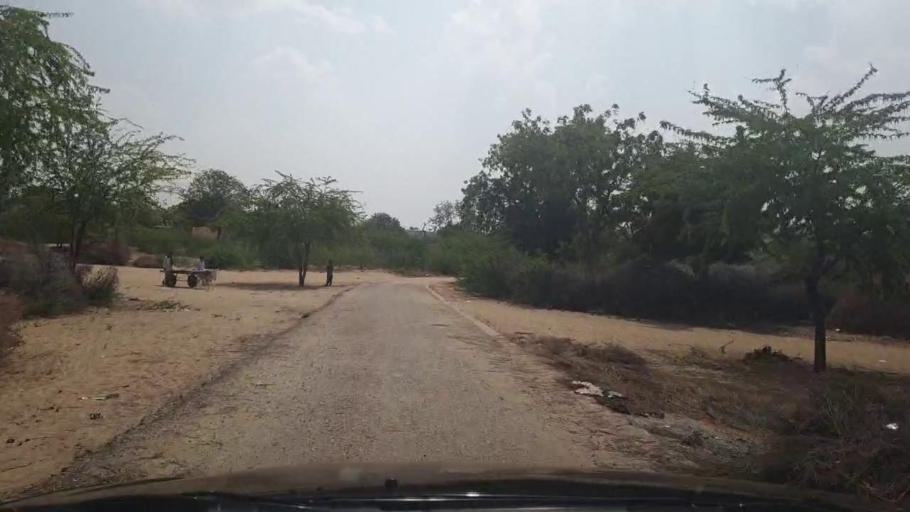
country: PK
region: Sindh
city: Islamkot
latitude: 24.9925
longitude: 70.4932
